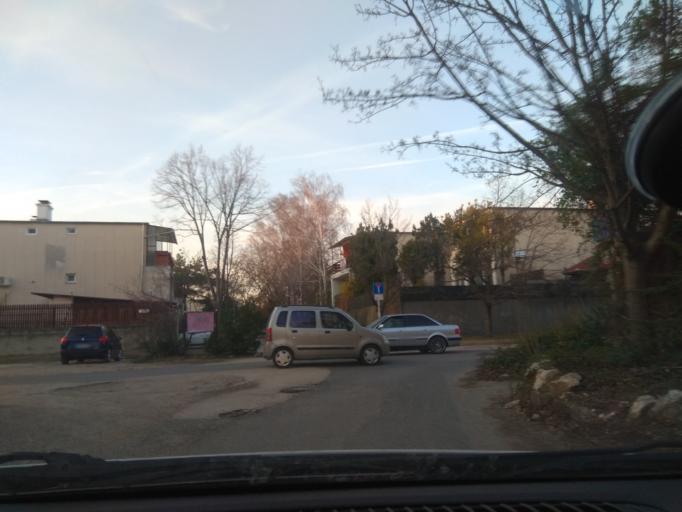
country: HU
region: Pest
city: Szigetszentmiklos
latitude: 47.3448
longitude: 19.0340
